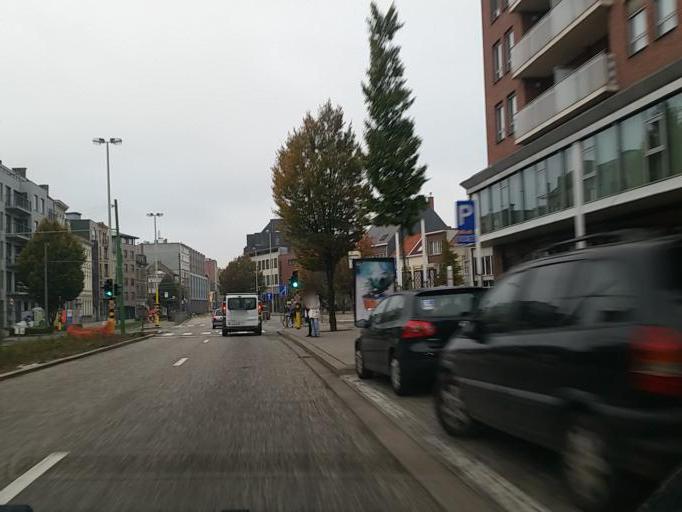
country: BE
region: Flanders
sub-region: Provincie Antwerpen
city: Antwerpen
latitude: 51.1951
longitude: 4.4194
